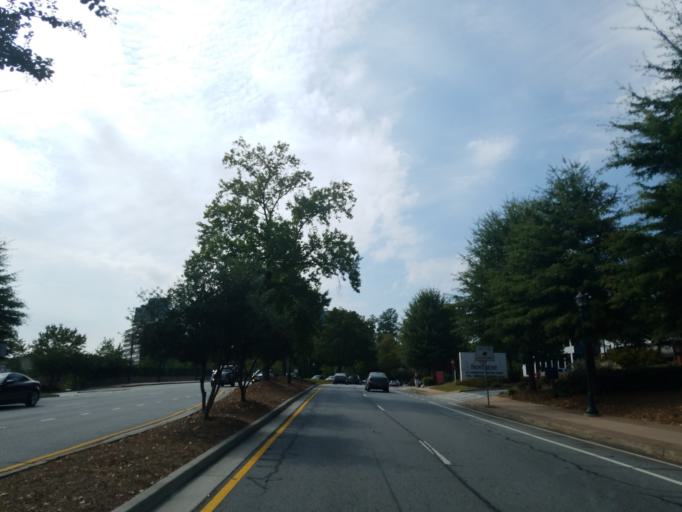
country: US
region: Georgia
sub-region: DeKalb County
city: Dunwoody
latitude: 33.9270
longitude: -84.3424
